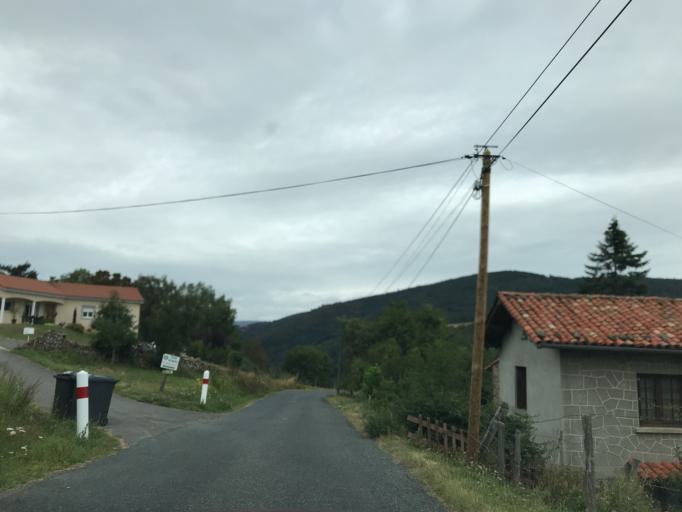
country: FR
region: Rhone-Alpes
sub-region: Departement de la Loire
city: Sail-sous-Couzan
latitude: 45.6800
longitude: 3.9038
